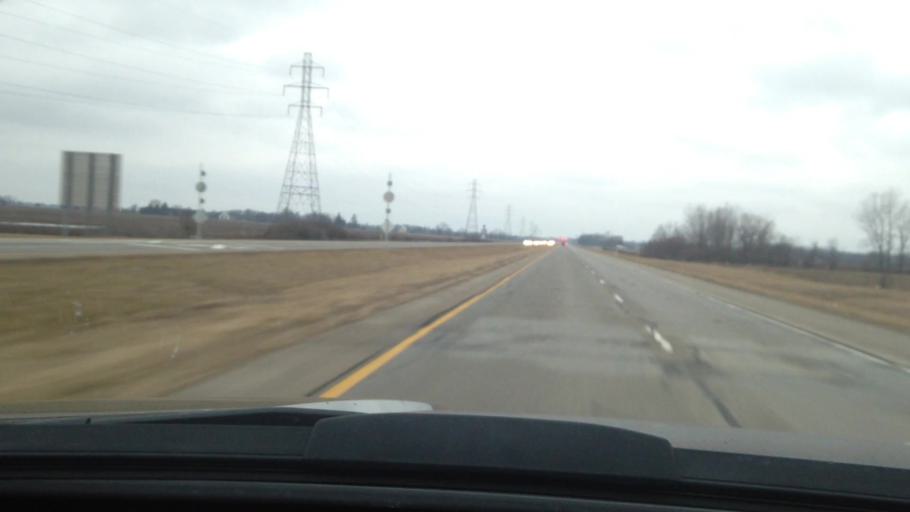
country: US
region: Indiana
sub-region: Delaware County
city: Muncie
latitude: 40.1423
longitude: -85.3920
